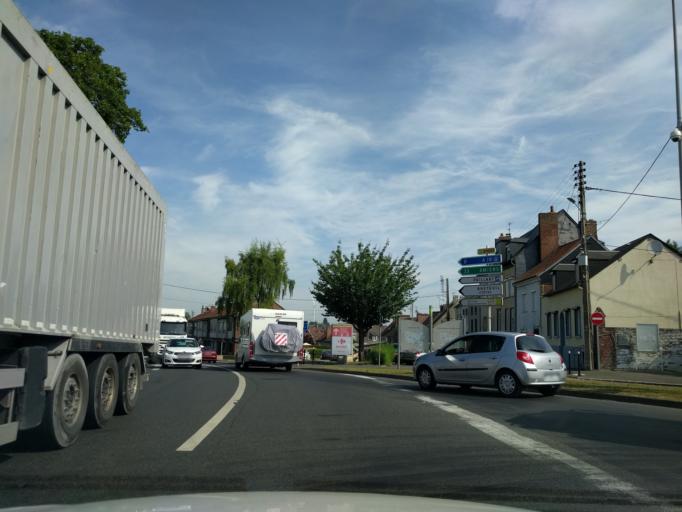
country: FR
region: Picardie
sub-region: Departement de l'Oise
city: Breteuil
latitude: 49.6296
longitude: 2.2939
